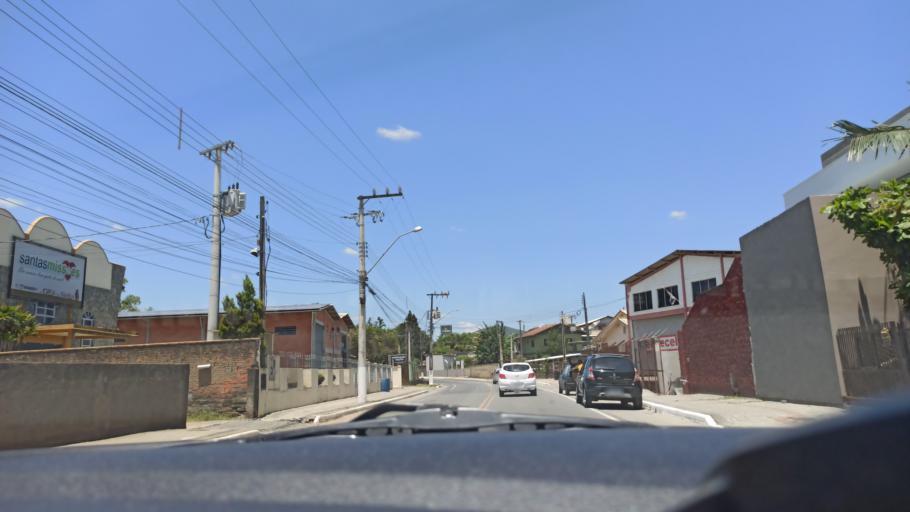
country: BR
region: Santa Catarina
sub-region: Indaial
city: Indaial
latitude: -26.8863
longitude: -49.2402
